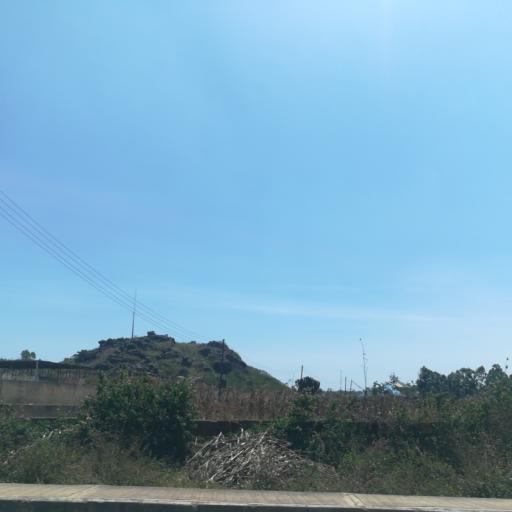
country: NG
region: Plateau
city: Bukuru
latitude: 9.8199
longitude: 8.8777
